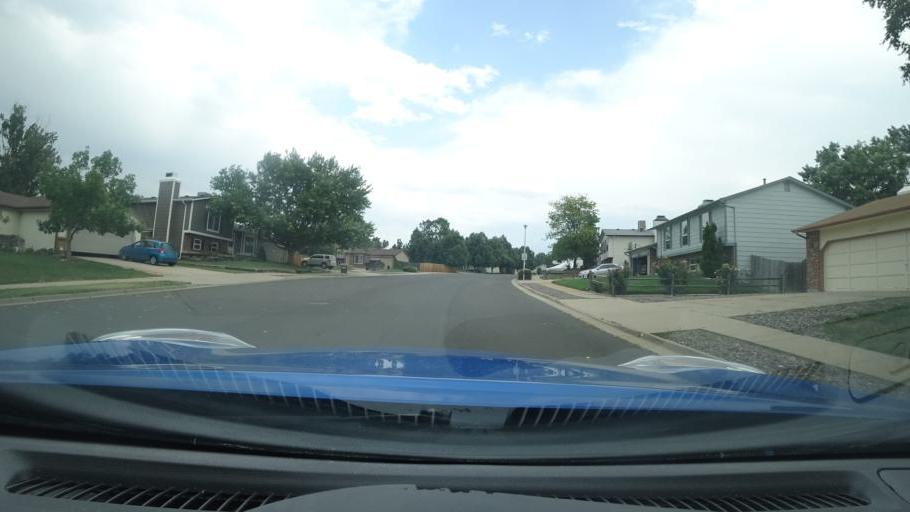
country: US
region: Colorado
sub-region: Adams County
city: Aurora
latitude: 39.6869
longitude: -104.7607
